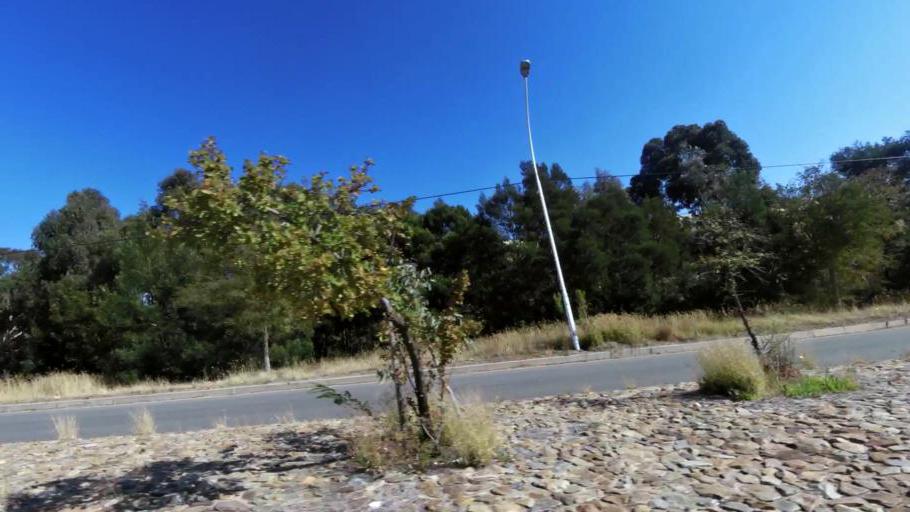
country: ZA
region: Gauteng
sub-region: City of Johannesburg Metropolitan Municipality
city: Johannesburg
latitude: -26.2444
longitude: 27.9750
